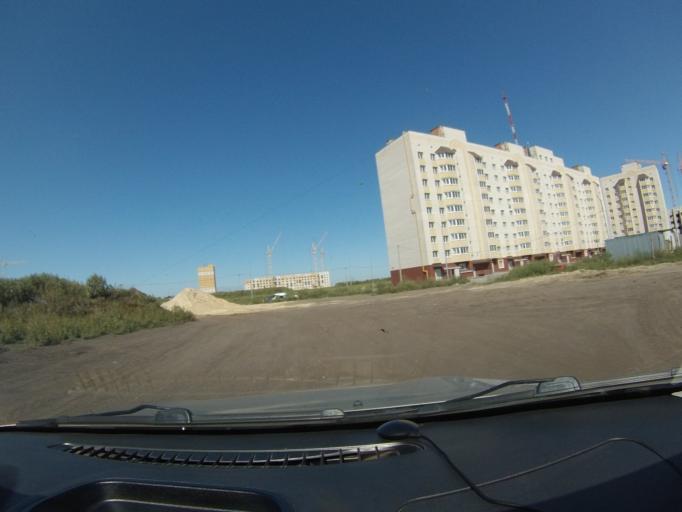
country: RU
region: Tambov
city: Tambov
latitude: 52.7753
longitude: 41.4098
